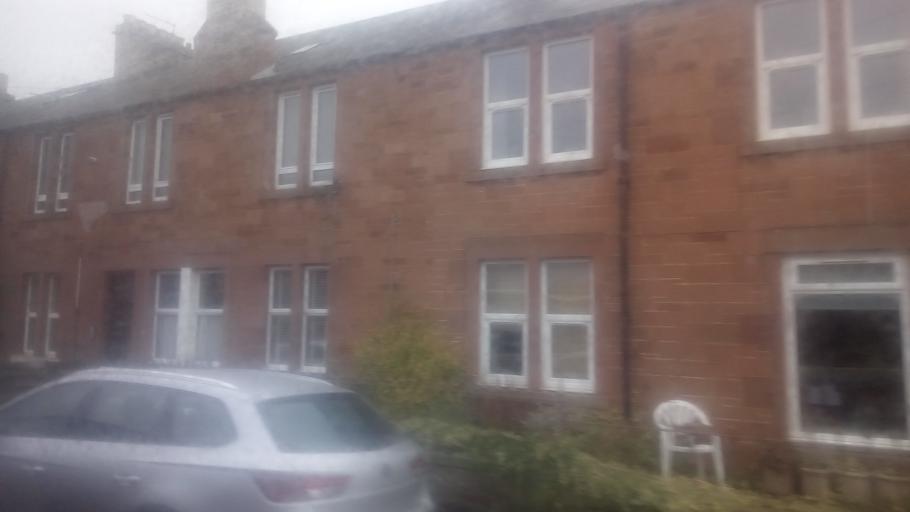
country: GB
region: Scotland
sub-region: The Scottish Borders
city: Newtown St Boswells
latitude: 55.5786
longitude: -2.6732
